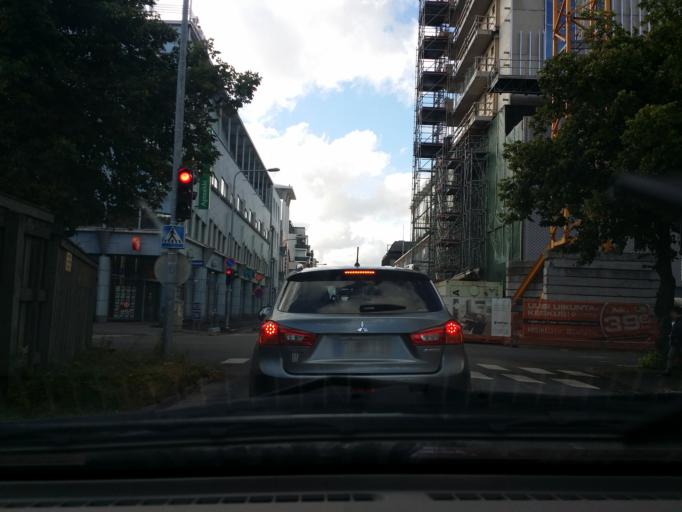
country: FI
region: Satakunta
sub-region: Pori
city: Pori
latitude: 61.4828
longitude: 21.7986
